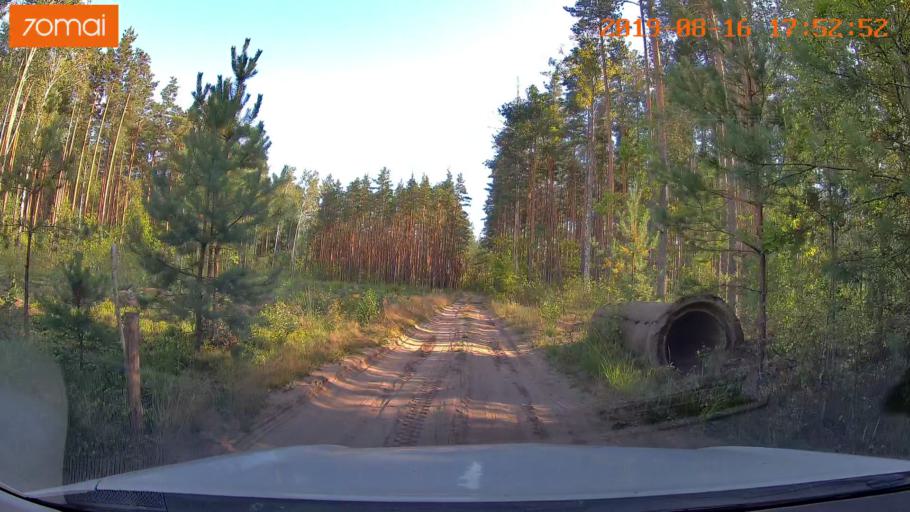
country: BY
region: Mogilev
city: Asipovichy
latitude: 53.2257
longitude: 28.6589
